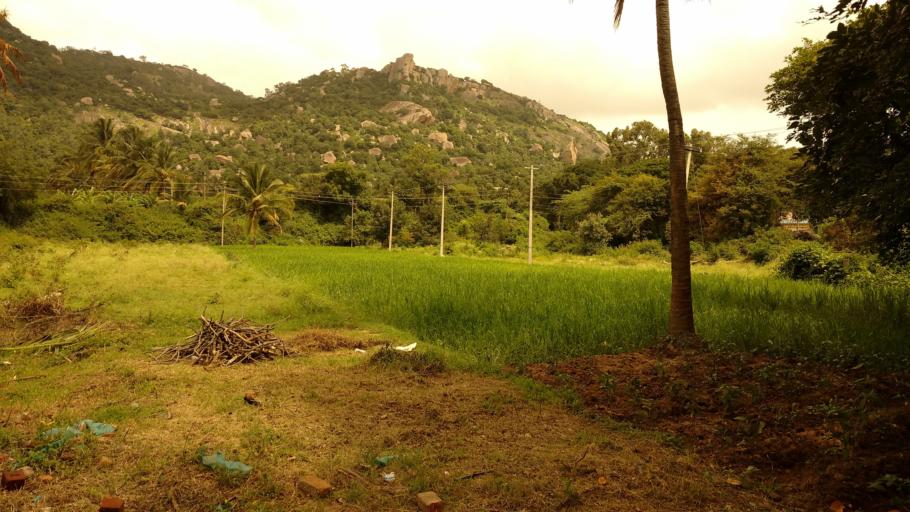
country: IN
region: Karnataka
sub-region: Tumkur
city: Tumkur
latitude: 13.3847
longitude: 77.2027
